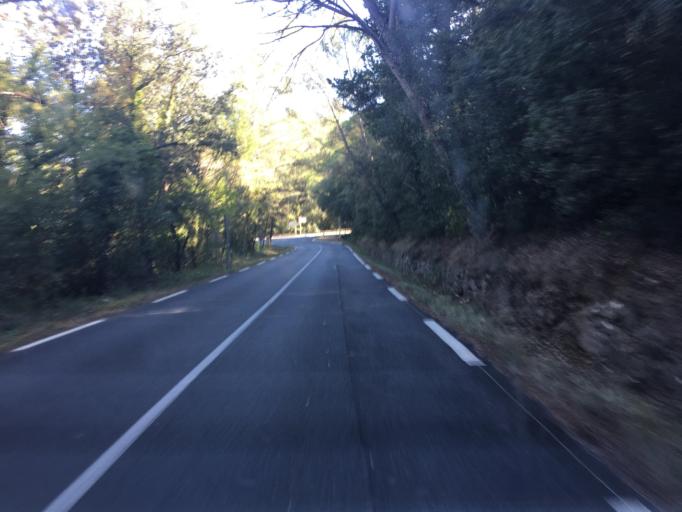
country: FR
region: Languedoc-Roussillon
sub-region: Departement de l'Herault
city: Nebian
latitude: 43.6097
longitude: 3.3958
